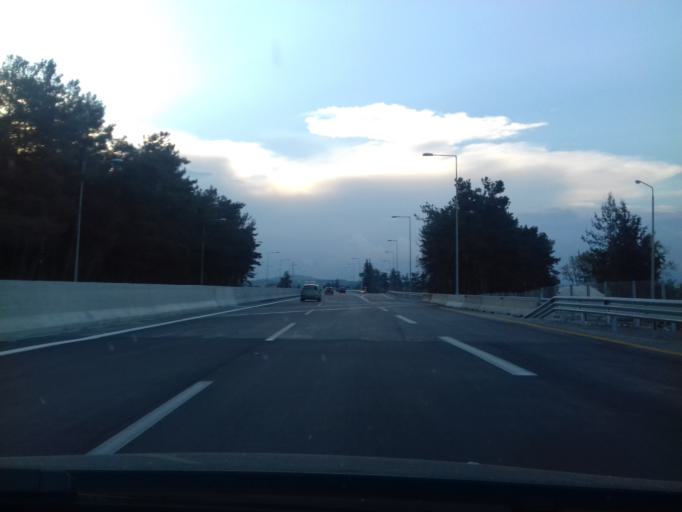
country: GR
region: West Greece
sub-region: Nomos Achaias
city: Temeni
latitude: 38.2196
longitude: 22.1057
